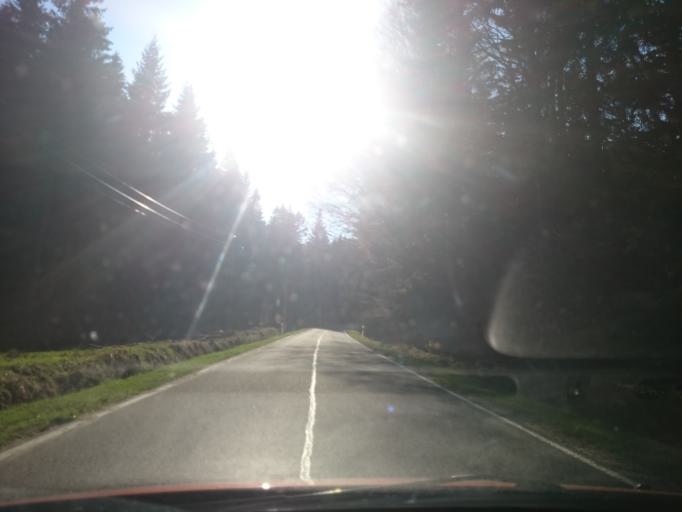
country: PL
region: Lower Silesian Voivodeship
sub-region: Powiat klodzki
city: Duszniki-Zdroj
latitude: 50.3246
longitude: 16.4150
